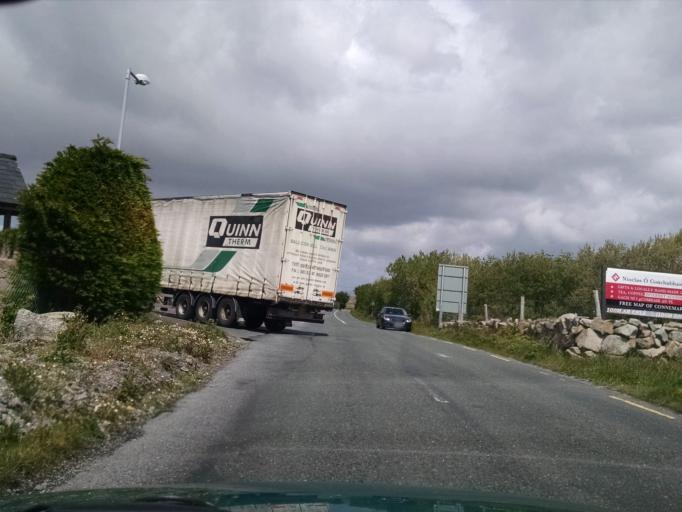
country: IE
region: Connaught
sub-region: County Galway
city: Oughterard
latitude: 53.2907
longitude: -9.5492
